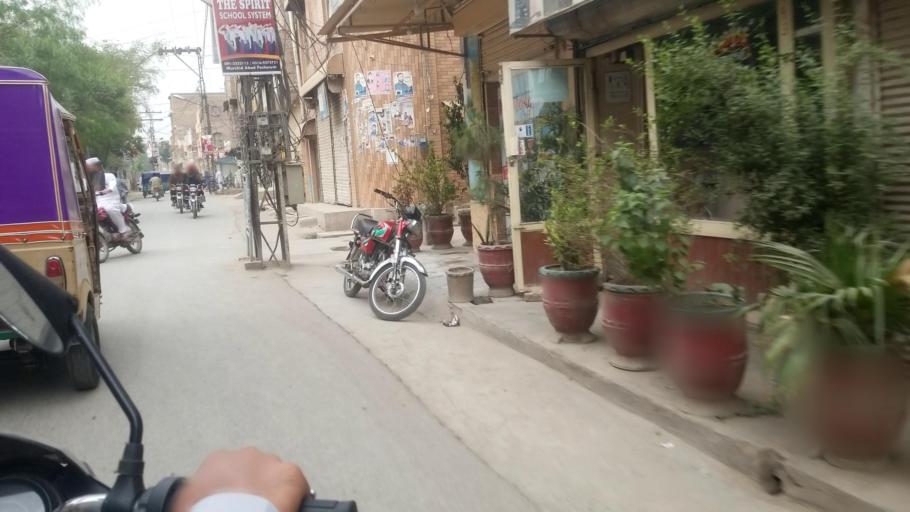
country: PK
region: Khyber Pakhtunkhwa
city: Peshawar
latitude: 33.9985
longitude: 71.5652
